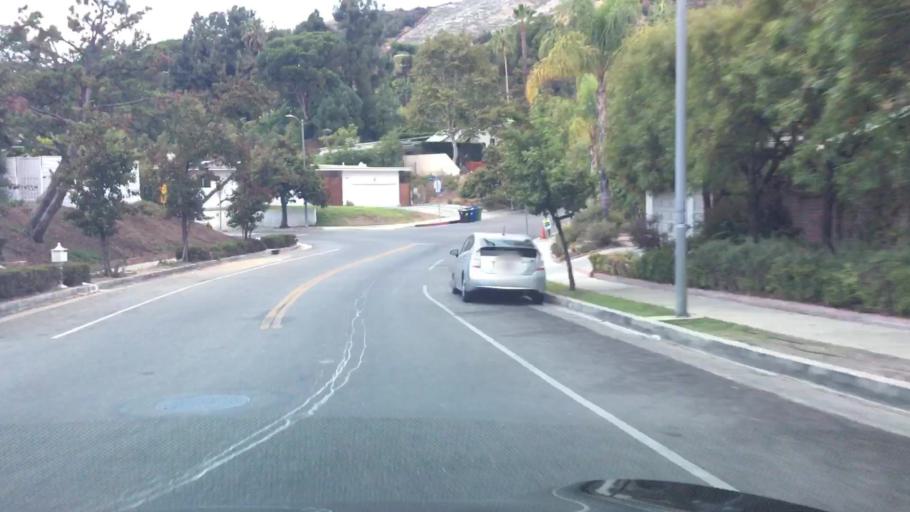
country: US
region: California
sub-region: Los Angeles County
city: Universal City
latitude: 34.1275
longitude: -118.3268
